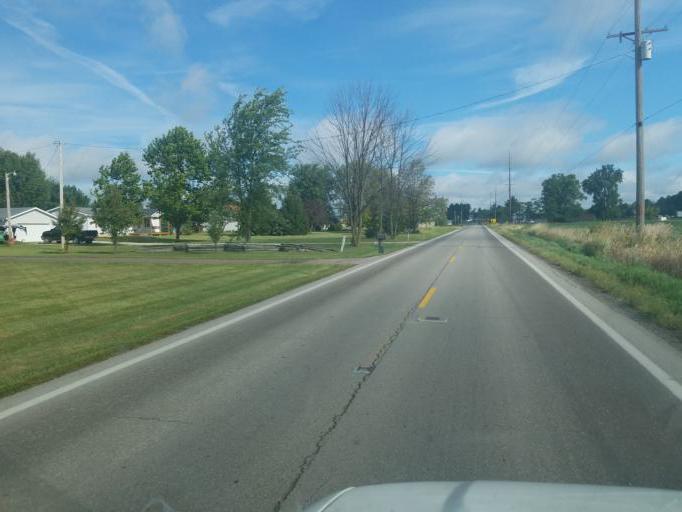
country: US
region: Ohio
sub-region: Wayne County
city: West Salem
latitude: 40.9879
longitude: -82.1100
